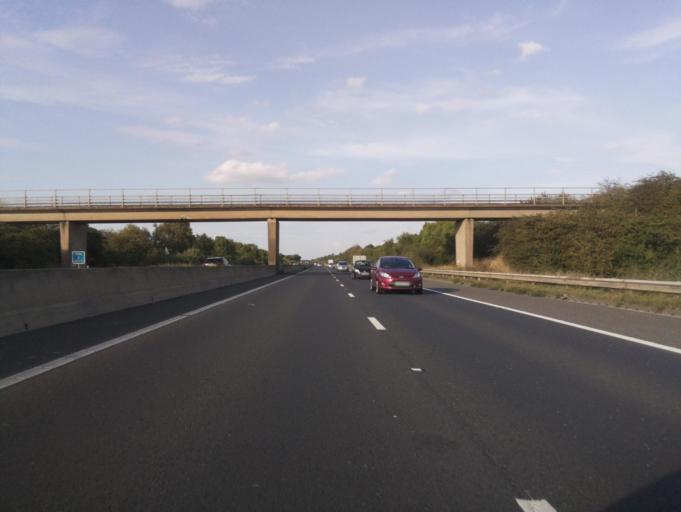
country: GB
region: England
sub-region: Doncaster
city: Hatfield
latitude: 53.5563
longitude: -1.0055
